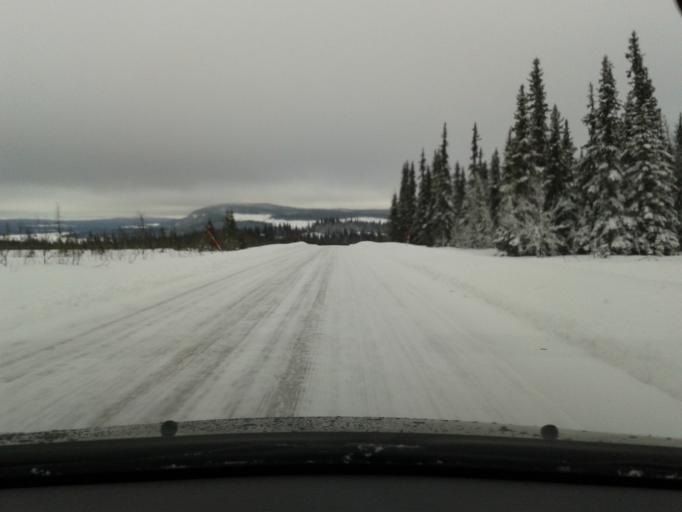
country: SE
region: Vaesterbotten
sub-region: Vilhelmina Kommun
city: Sjoberg
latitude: 65.0443
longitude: 15.9019
